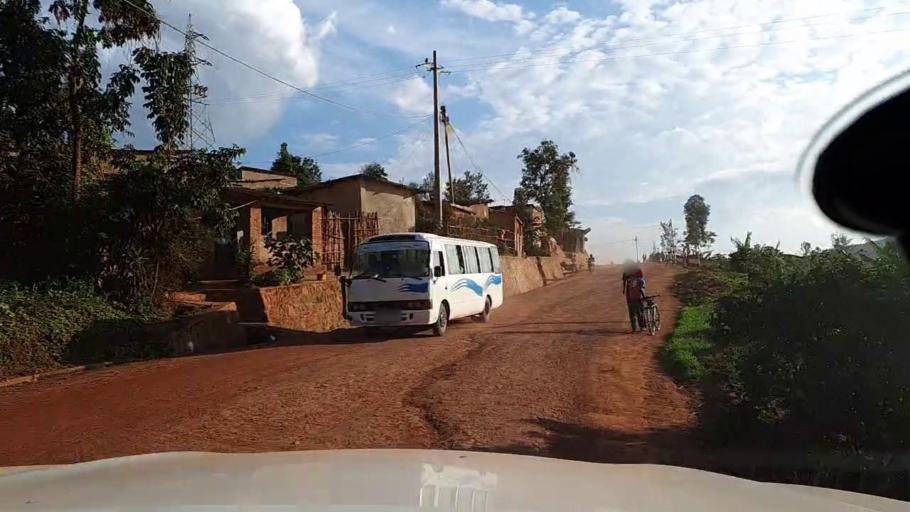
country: RW
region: Kigali
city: Kigali
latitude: -1.9393
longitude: 30.0012
